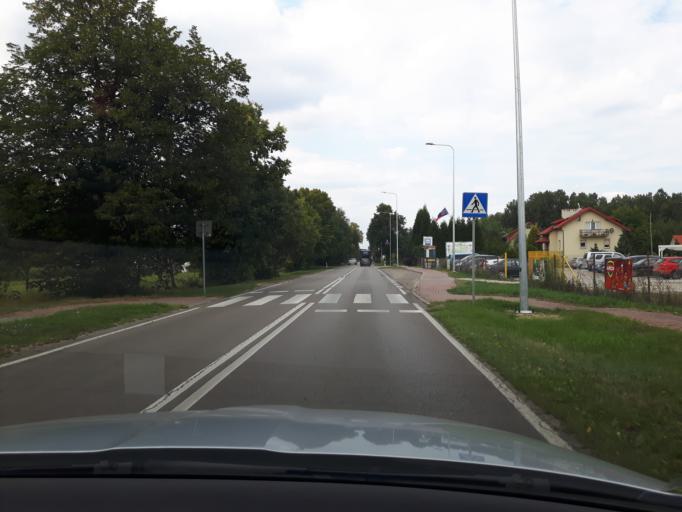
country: PL
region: Masovian Voivodeship
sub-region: Powiat legionowski
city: Nieporet
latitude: 52.4075
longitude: 21.0385
